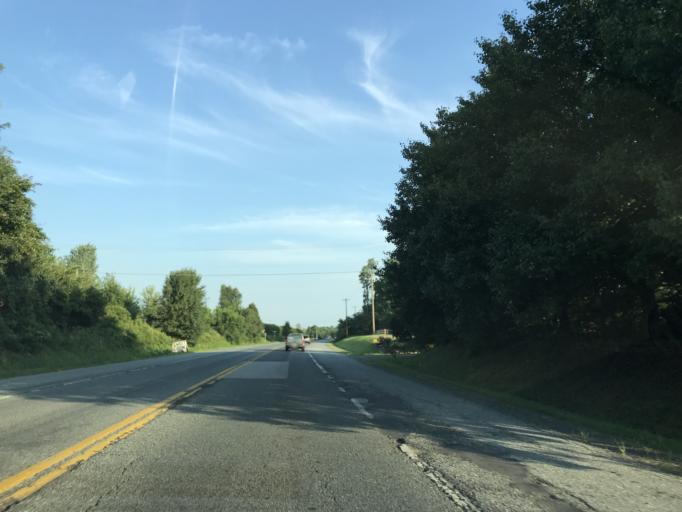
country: US
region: Maryland
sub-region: Cecil County
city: North East
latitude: 39.6704
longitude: -75.9590
